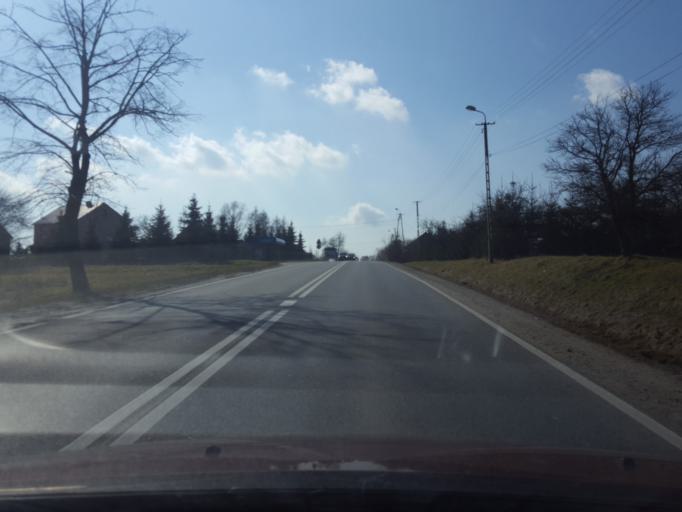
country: PL
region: Lesser Poland Voivodeship
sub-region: Powiat brzeski
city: Gnojnik
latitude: 49.8738
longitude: 20.6175
